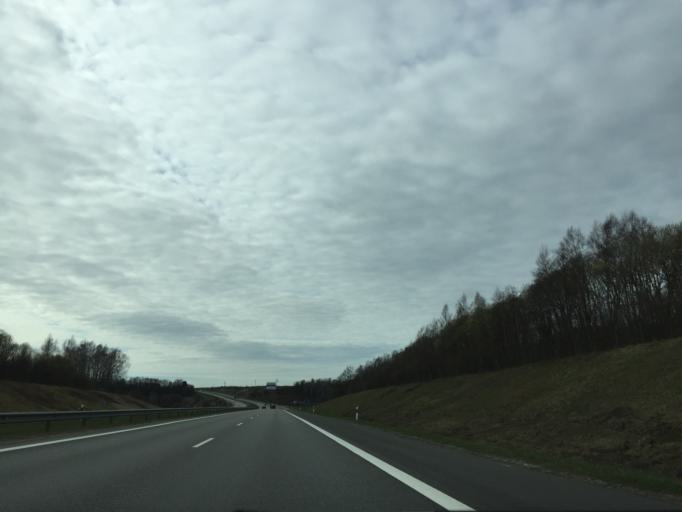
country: LT
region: Klaipedos apskritis
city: Gargzdai
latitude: 55.7251
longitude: 21.4233
